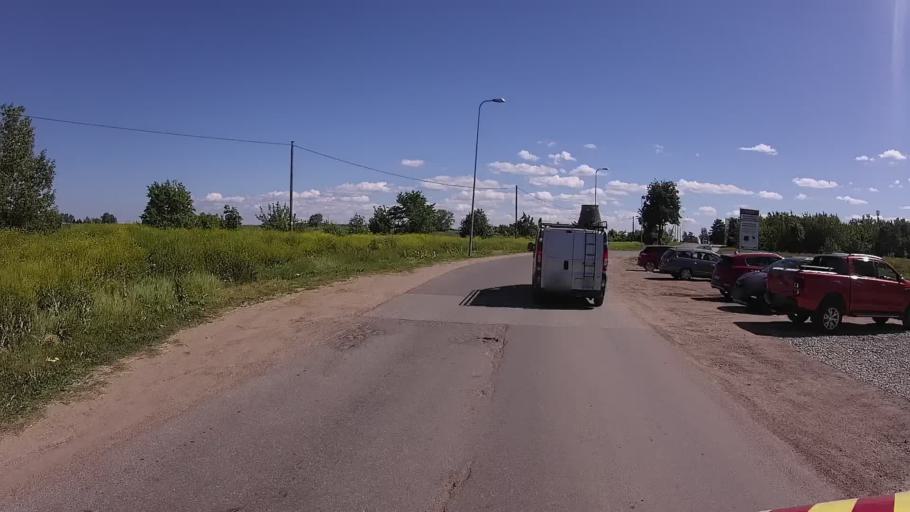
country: EE
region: Ida-Virumaa
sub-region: Kohtla-Jaerve linn
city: Kohtla-Jarve
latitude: 59.4050
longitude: 27.2976
